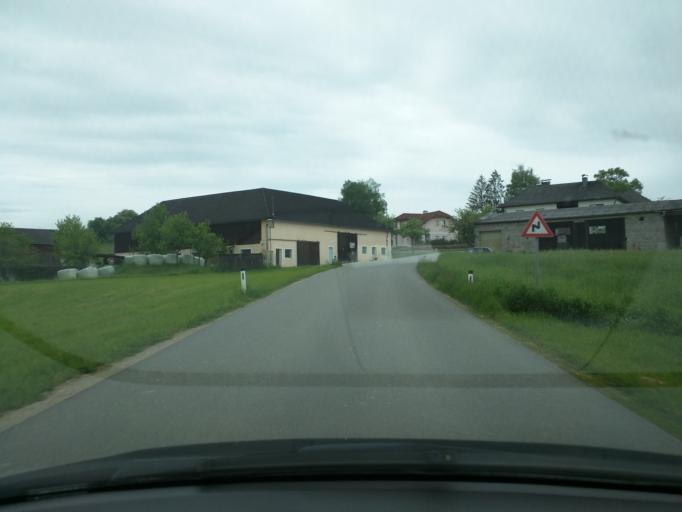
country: AT
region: Lower Austria
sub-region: Politischer Bezirk Melk
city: Blindenmarkt
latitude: 48.1394
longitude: 14.9745
